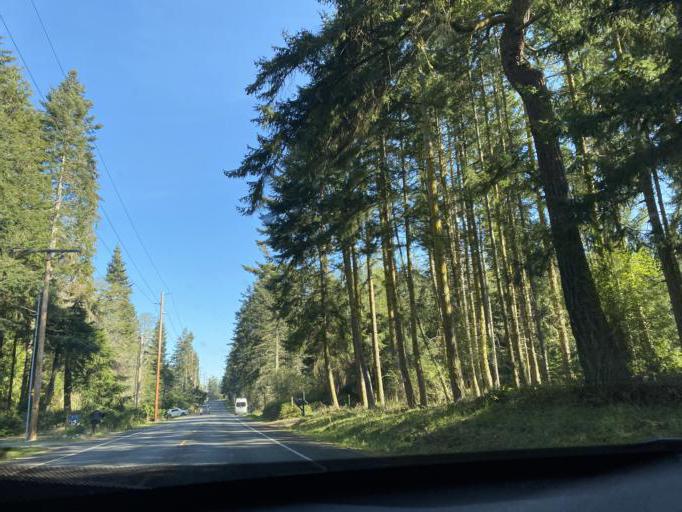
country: US
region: Washington
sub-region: Island County
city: Freeland
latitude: 48.0742
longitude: -122.6048
